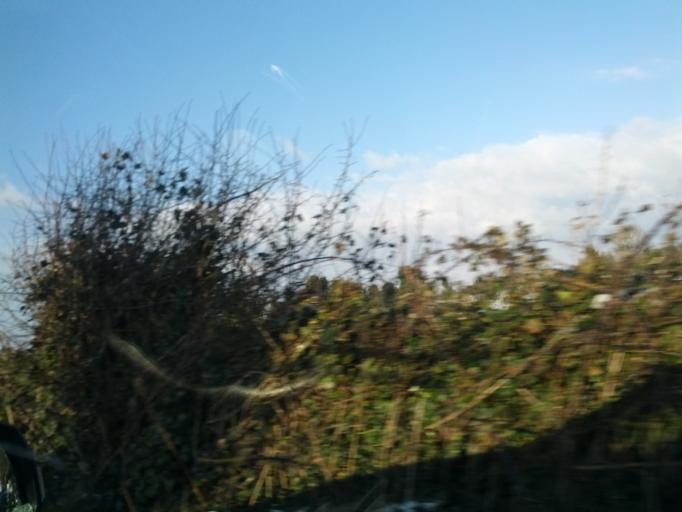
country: IE
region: Connaught
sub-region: County Galway
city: Athenry
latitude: 53.1947
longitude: -8.7348
